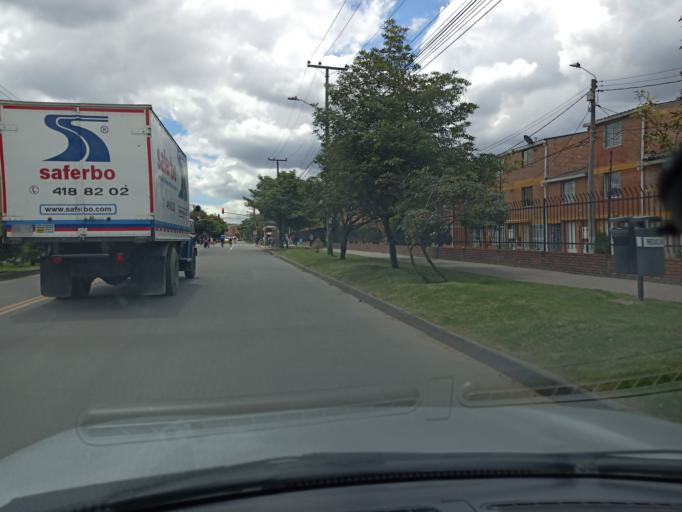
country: CO
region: Cundinamarca
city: Funza
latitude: 4.6705
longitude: -74.1556
